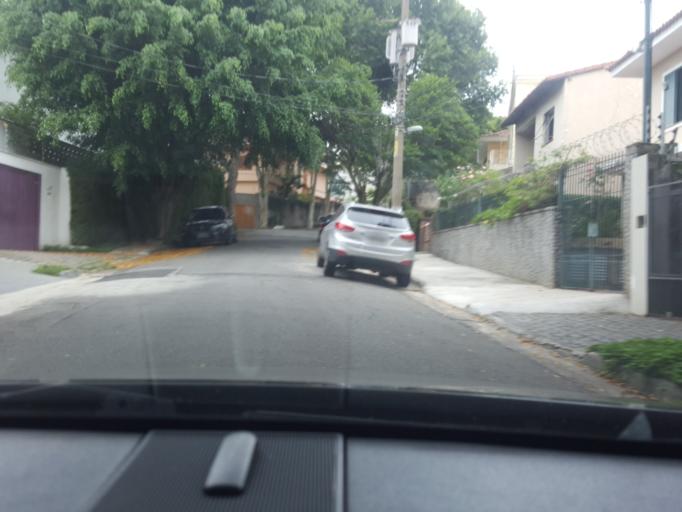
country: BR
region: Sao Paulo
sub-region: Sao Paulo
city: Sao Paulo
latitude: -23.5506
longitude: -46.6694
